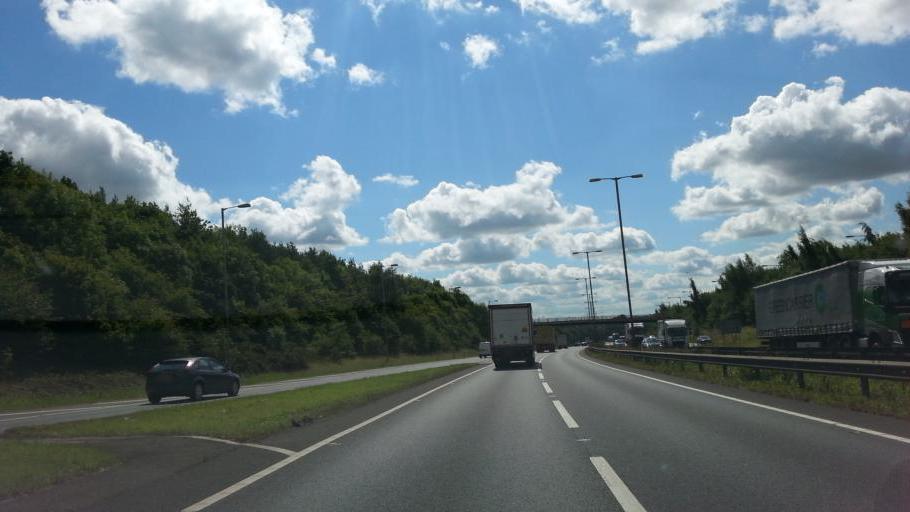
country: GB
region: England
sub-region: Northamptonshire
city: Kettering
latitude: 52.4052
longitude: -0.7521
